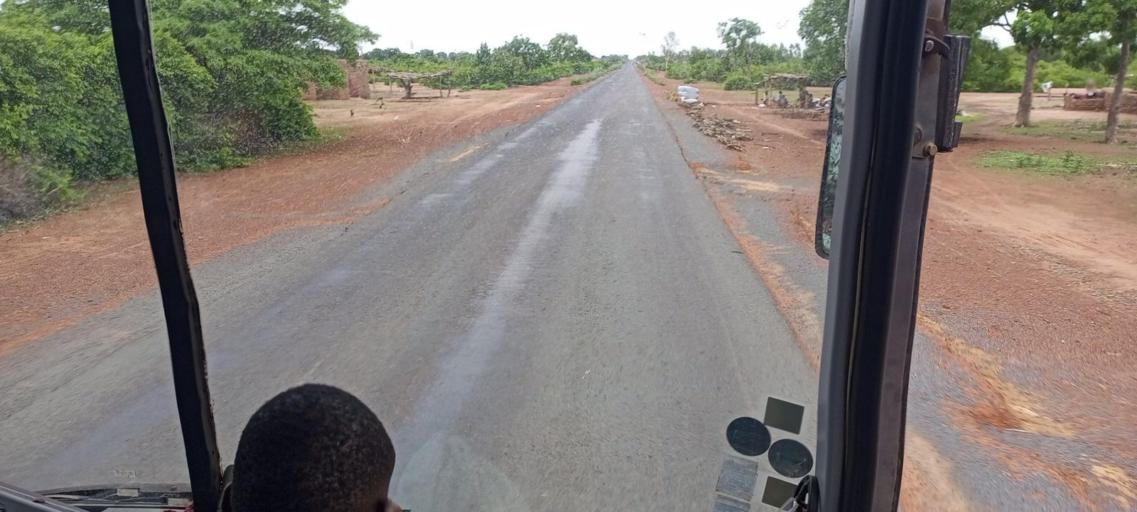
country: ML
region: Sikasso
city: Koutiala
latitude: 12.5447
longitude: -5.5790
